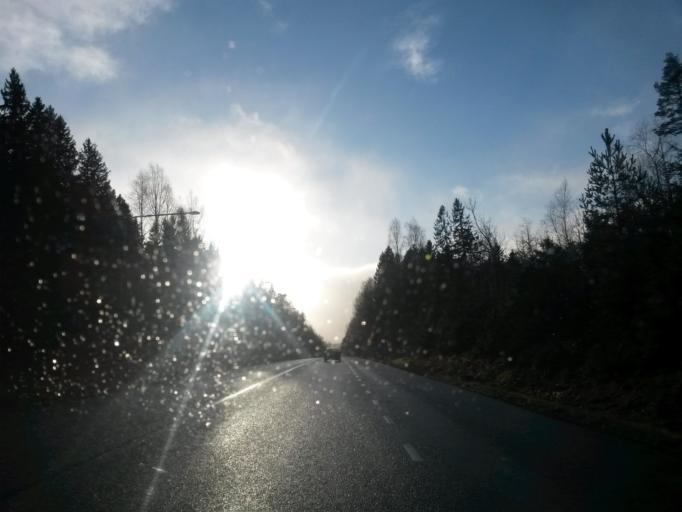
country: SE
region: Vaestra Goetaland
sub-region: Boras Kommun
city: Boras
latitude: 57.7649
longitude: 12.9700
